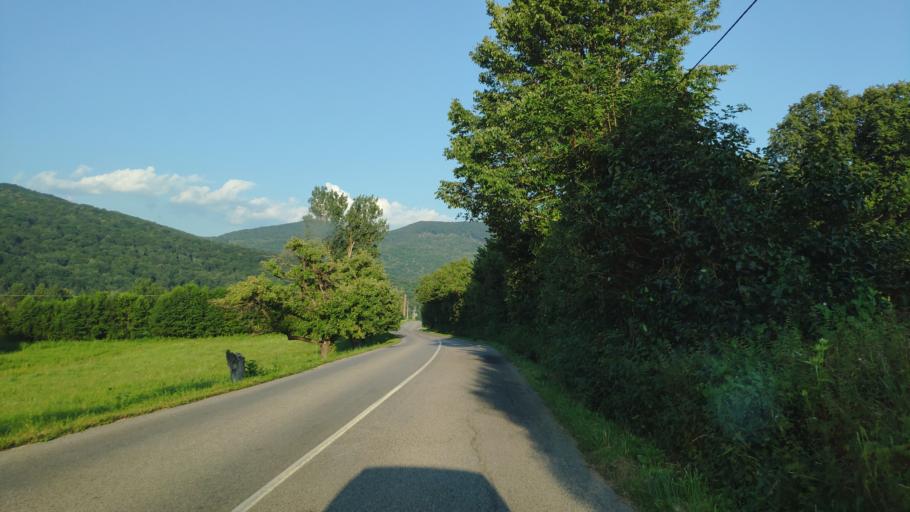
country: SK
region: Kosicky
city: Dobsina
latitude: 48.6772
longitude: 20.3478
